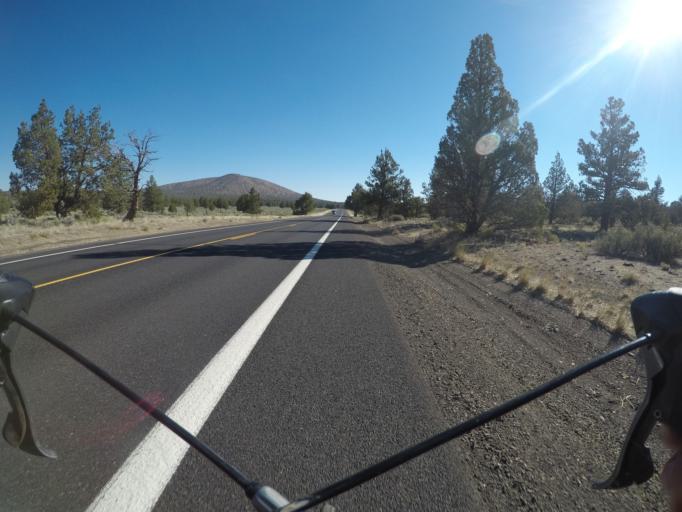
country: US
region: Oregon
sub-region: Deschutes County
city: Redmond
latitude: 44.2266
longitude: -121.3080
